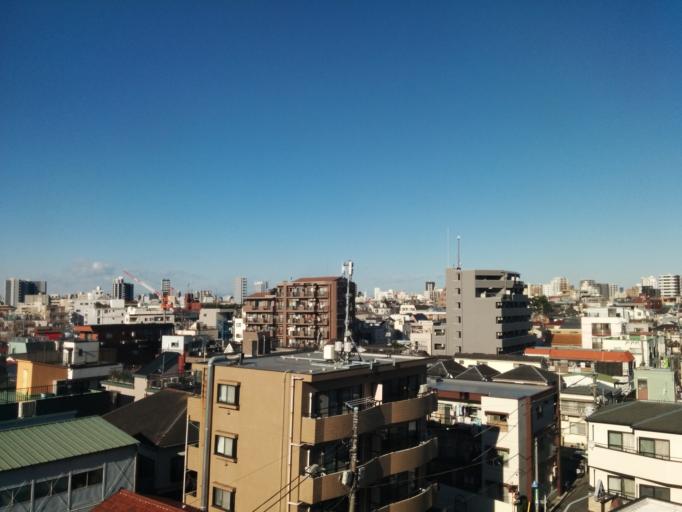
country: JP
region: Kanagawa
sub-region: Kawasaki-shi
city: Kawasaki
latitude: 35.6018
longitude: 139.7215
